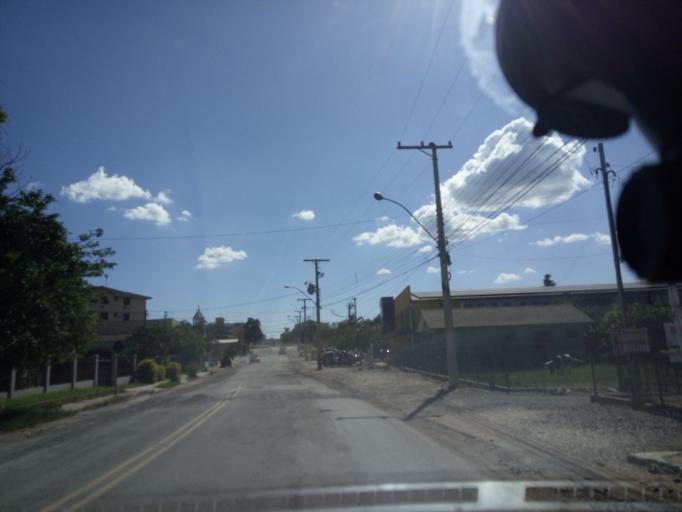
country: BR
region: Rio Grande do Sul
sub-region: Santa Maria
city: Santa Maria
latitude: -29.6975
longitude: -53.7312
